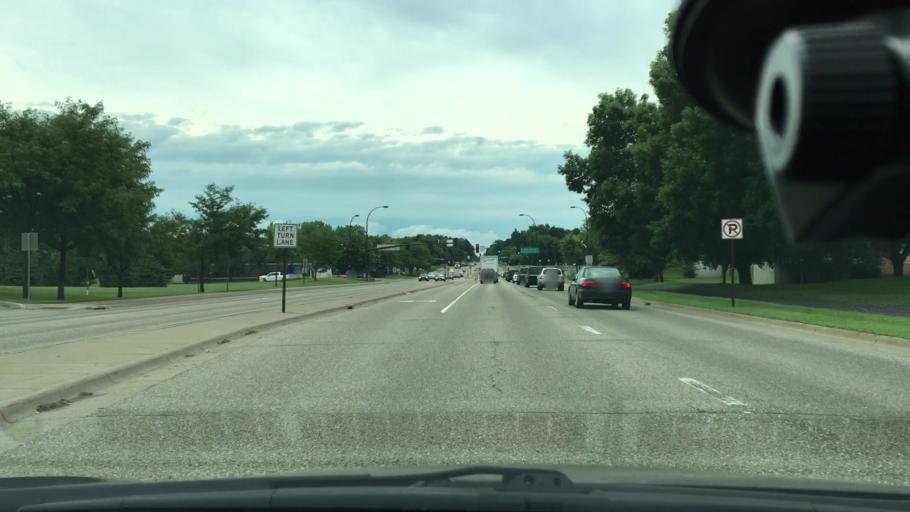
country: US
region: Minnesota
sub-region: Hennepin County
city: Maple Grove
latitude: 45.0814
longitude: -93.4313
